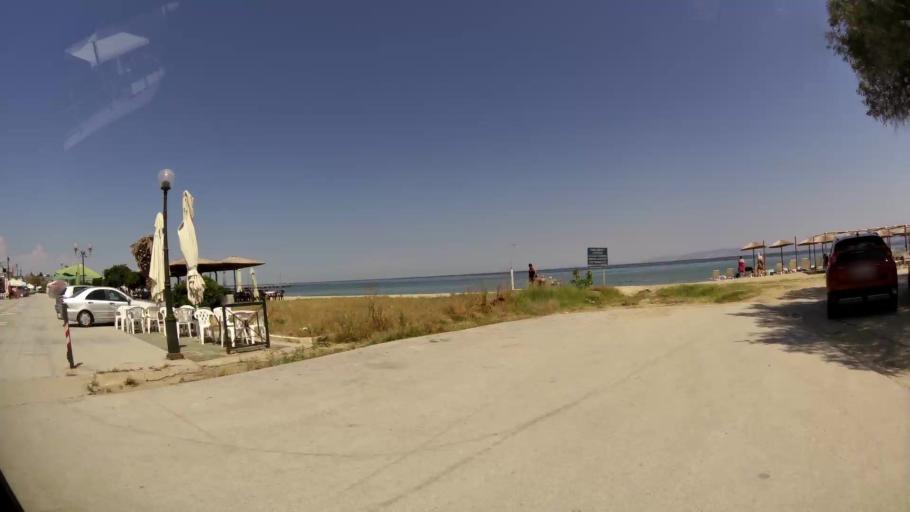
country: GR
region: Central Macedonia
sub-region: Nomos Thessalonikis
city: Agia Triada
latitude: 40.5008
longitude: 22.8783
